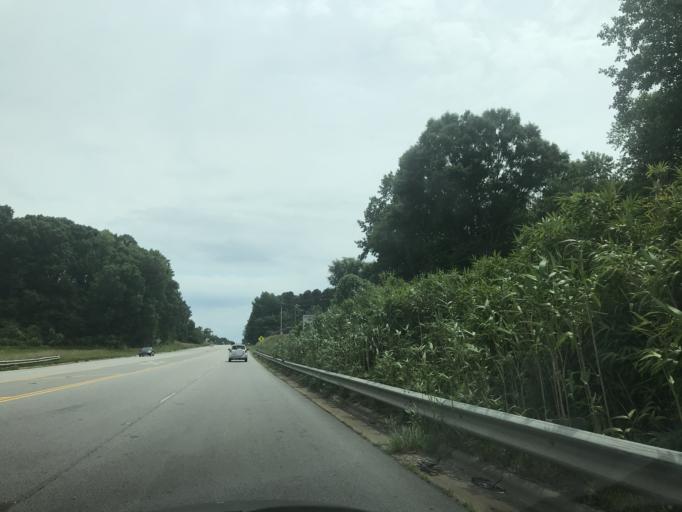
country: US
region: North Carolina
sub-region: Vance County
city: South Henderson
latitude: 36.2274
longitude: -78.4422
